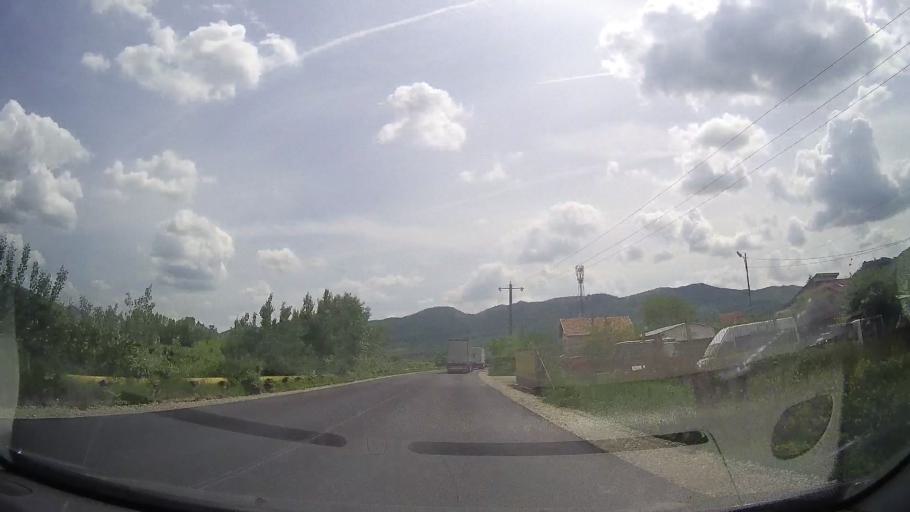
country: RO
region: Valcea
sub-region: Oras Calimanesti
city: Jiblea Veche
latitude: 45.2376
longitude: 24.3452
